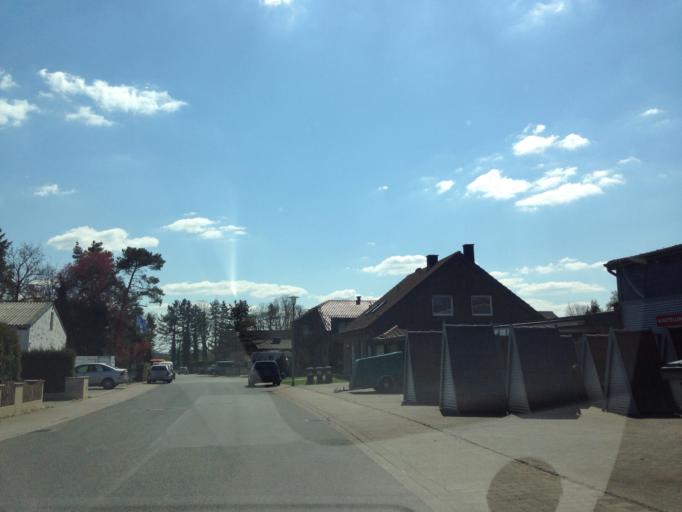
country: DE
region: North Rhine-Westphalia
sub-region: Regierungsbezirk Munster
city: Muenster
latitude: 51.8898
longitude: 7.5944
